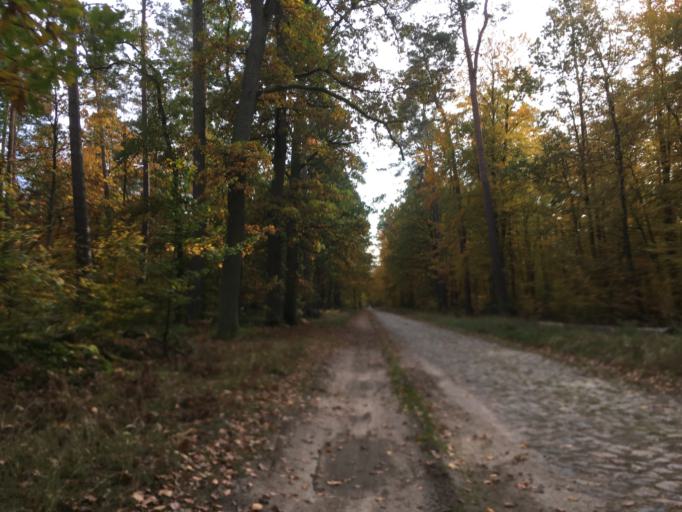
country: DE
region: Brandenburg
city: Templin
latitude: 52.9869
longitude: 13.4799
